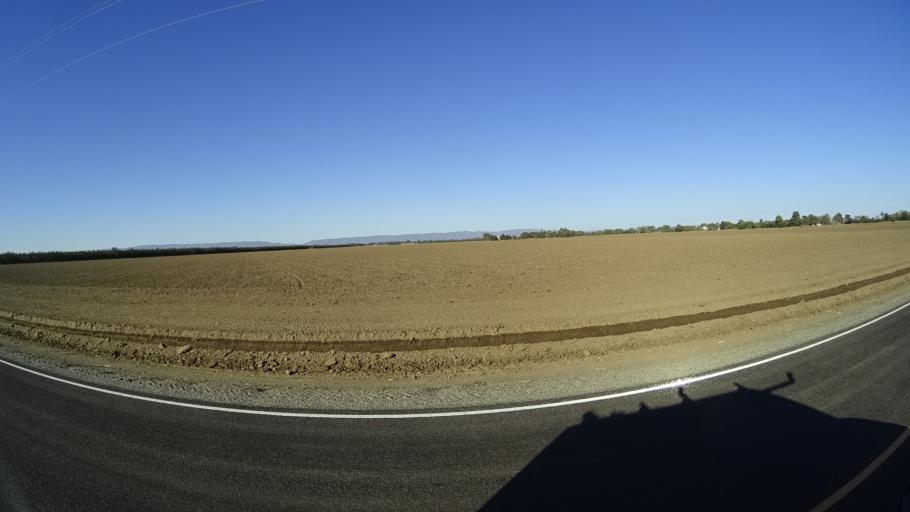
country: US
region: California
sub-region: Yolo County
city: Davis
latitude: 38.5856
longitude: -121.7857
